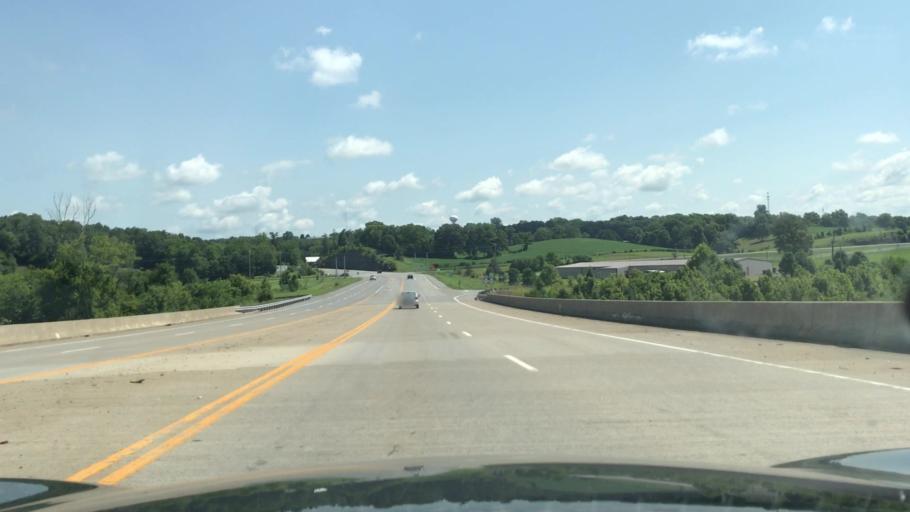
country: US
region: Kentucky
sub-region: Adair County
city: Columbia
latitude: 37.0863
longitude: -85.3234
